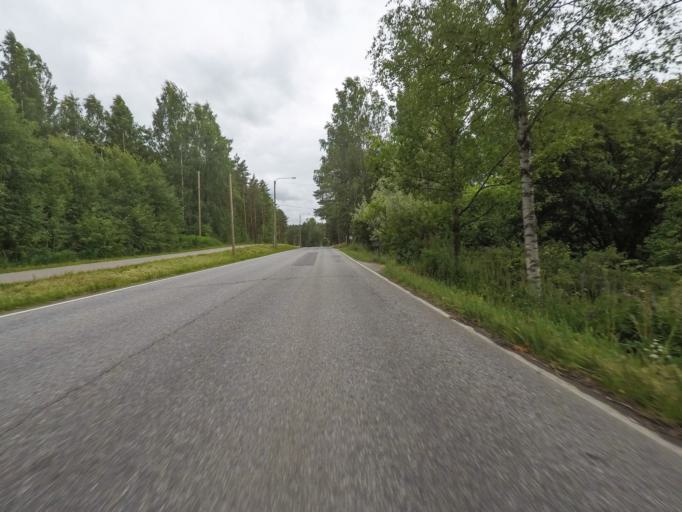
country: FI
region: Varsinais-Suomi
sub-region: Salo
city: Muurla
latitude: 60.3686
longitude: 23.3025
